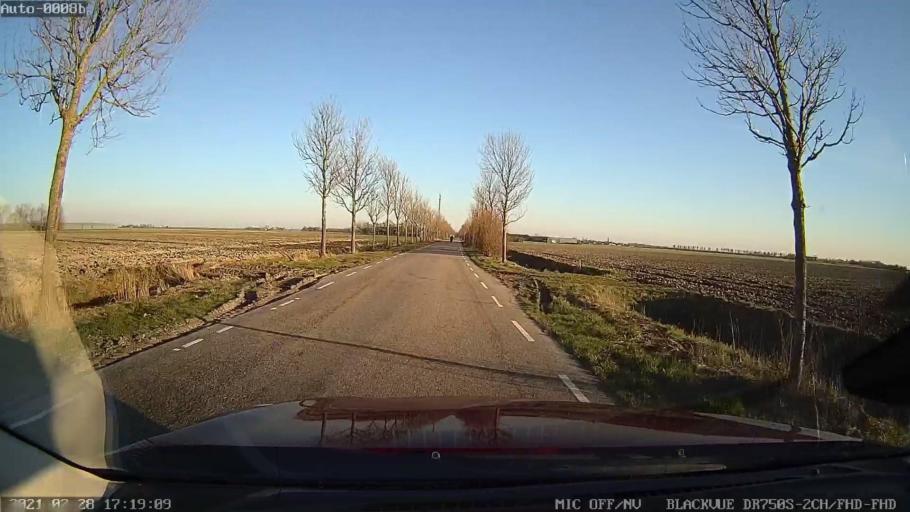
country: NL
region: South Holland
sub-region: Gemeente Goeree-Overflakkee
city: Ouddorp
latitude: 51.6984
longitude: 3.9665
